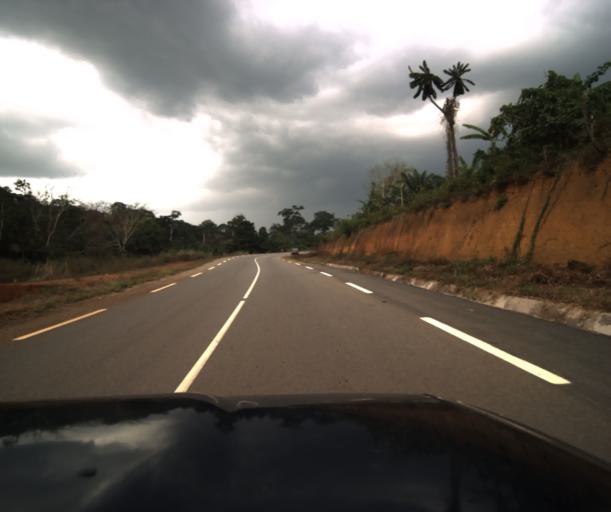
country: CM
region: Centre
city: Mbankomo
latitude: 3.6586
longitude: 11.3412
